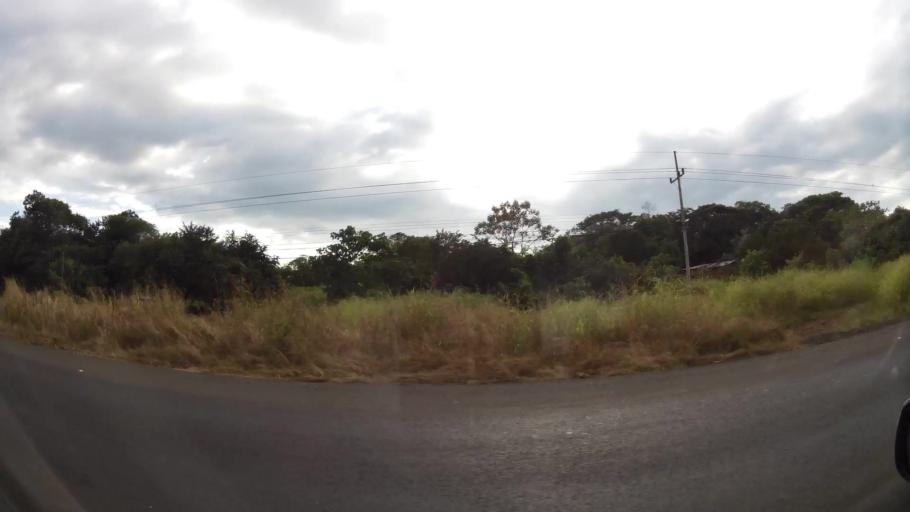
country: CR
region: Puntarenas
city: Esparza
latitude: 9.8981
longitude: -84.6569
